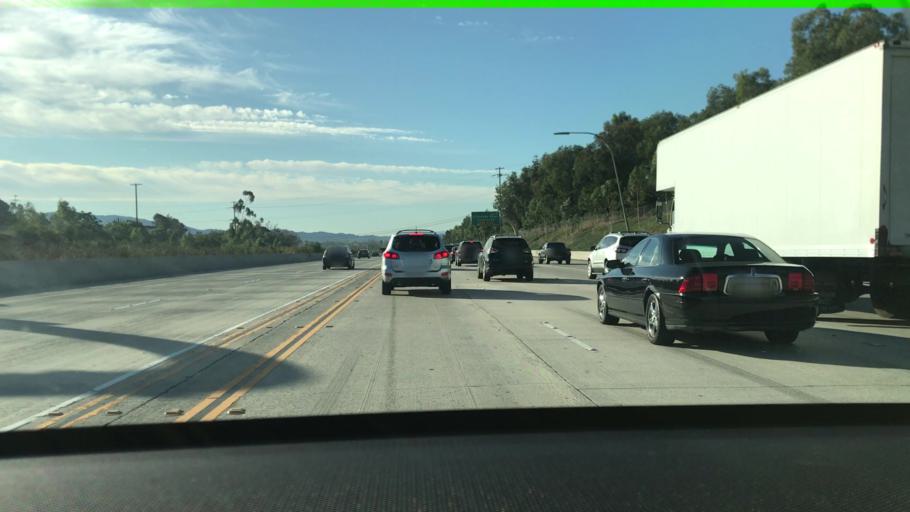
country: US
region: California
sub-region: San Diego County
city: Escondido
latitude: 33.1037
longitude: -117.0924
